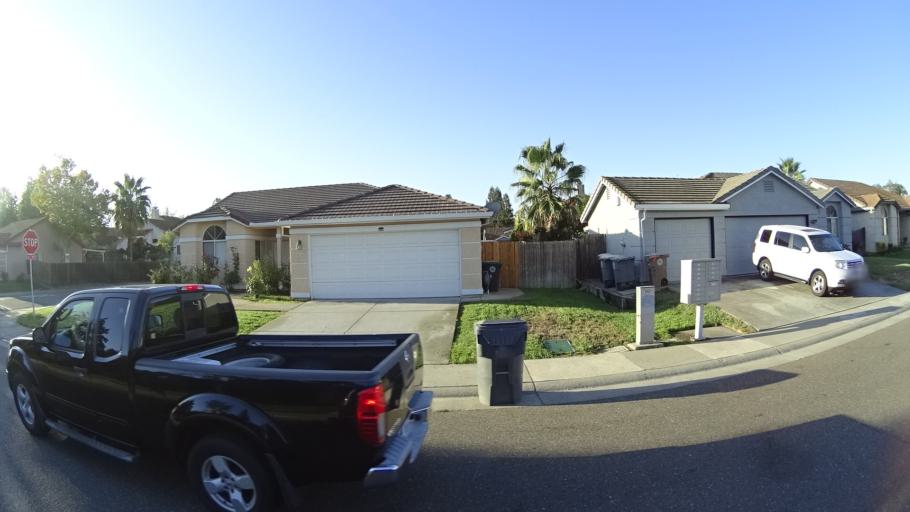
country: US
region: California
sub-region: Sacramento County
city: Laguna
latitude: 38.4273
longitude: -121.4513
